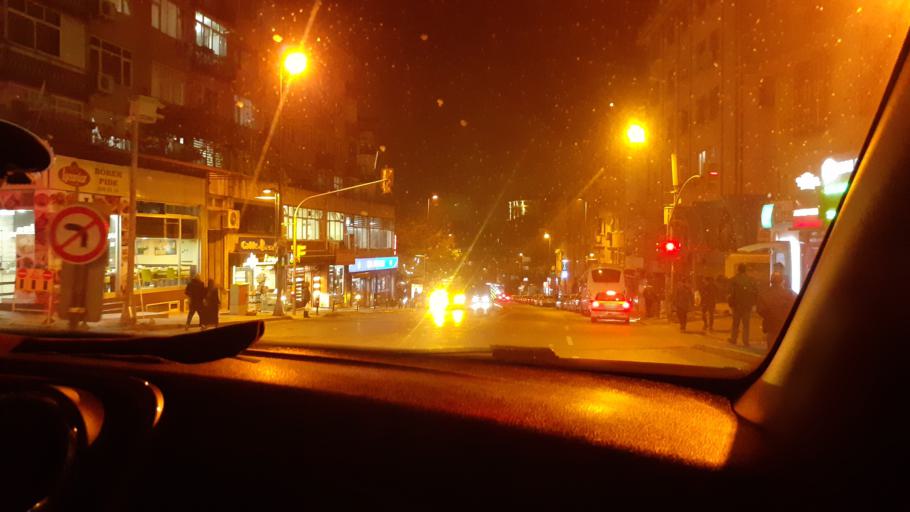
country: TR
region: Istanbul
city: UEskuedar
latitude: 41.0277
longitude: 29.0308
